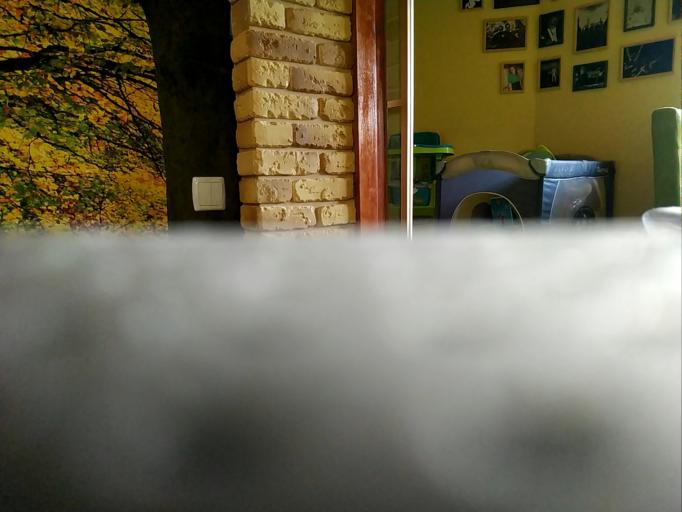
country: RU
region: Kaluga
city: Seredeyskiy
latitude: 54.0026
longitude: 35.3165
